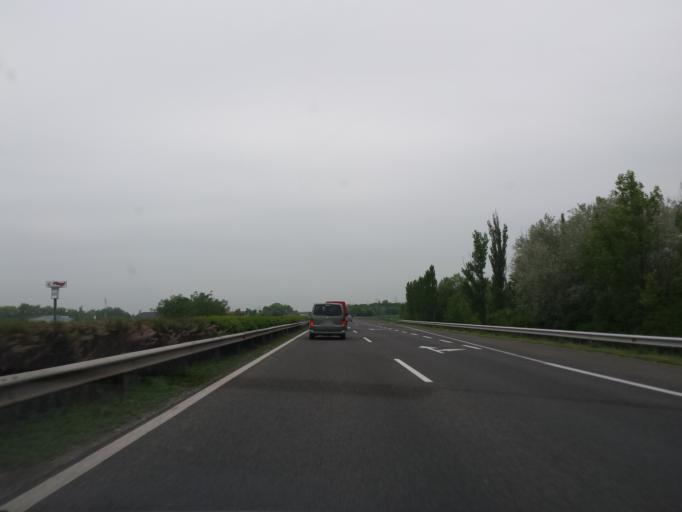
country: HU
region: Gyor-Moson-Sopron
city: Mosonszentmiklos
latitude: 47.7478
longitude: 17.4213
